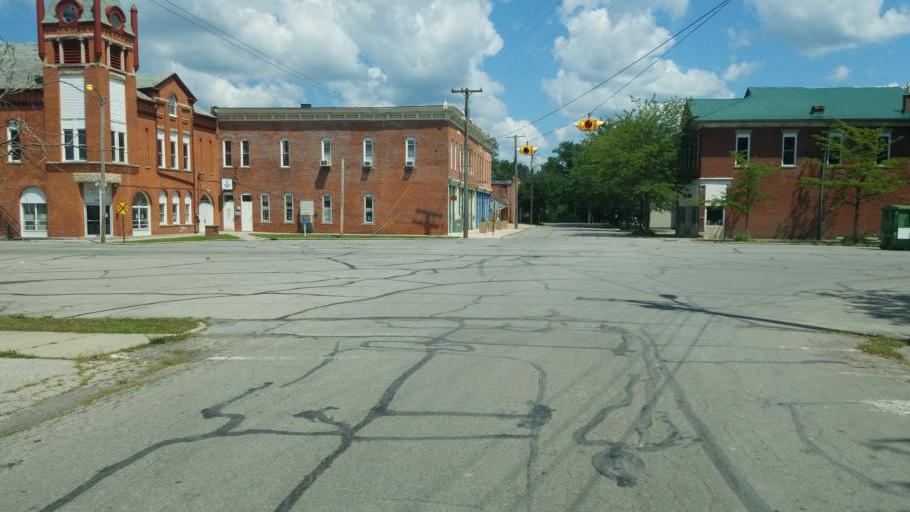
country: US
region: Ohio
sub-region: Morrow County
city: Cardington
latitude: 40.6366
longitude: -82.9692
